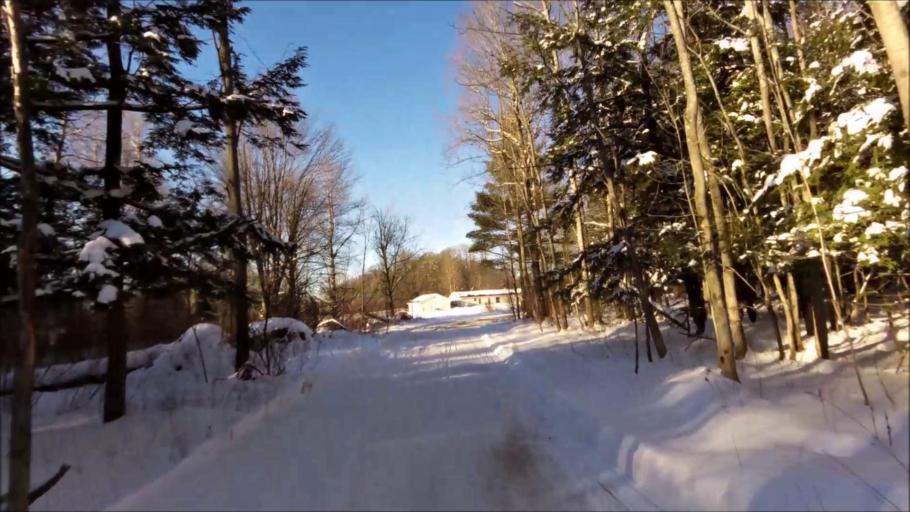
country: US
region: New York
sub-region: Chautauqua County
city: Mayville
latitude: 42.2836
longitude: -79.4343
